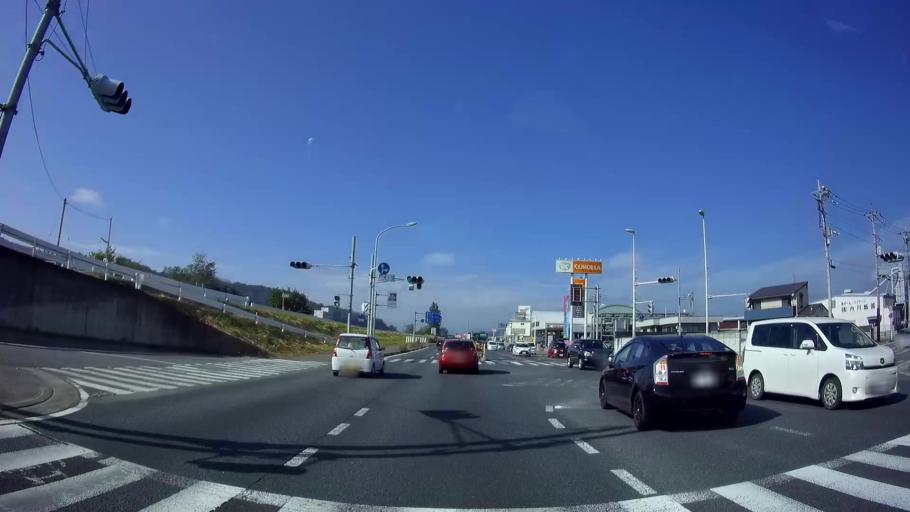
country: JP
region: Gunma
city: Annaka
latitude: 36.3336
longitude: 138.9521
